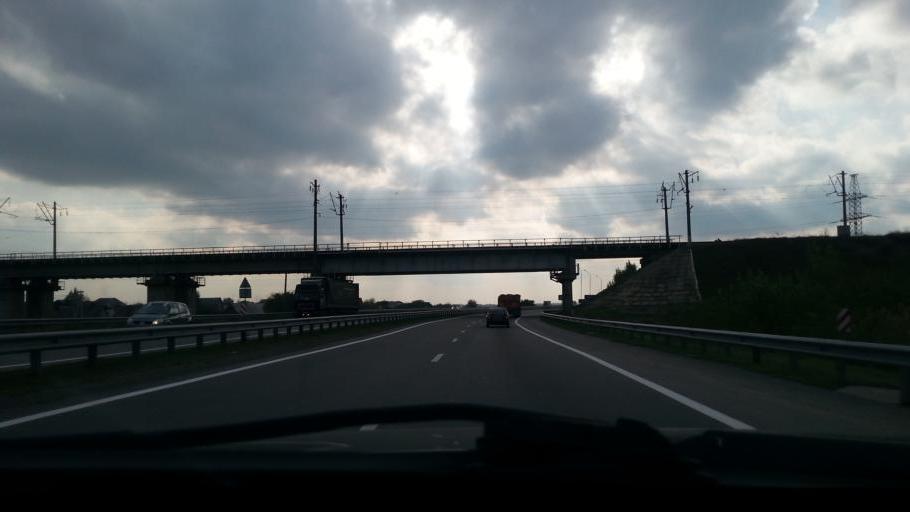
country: RU
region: Rostov
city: Bataysk
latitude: 47.1444
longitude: 39.6998
